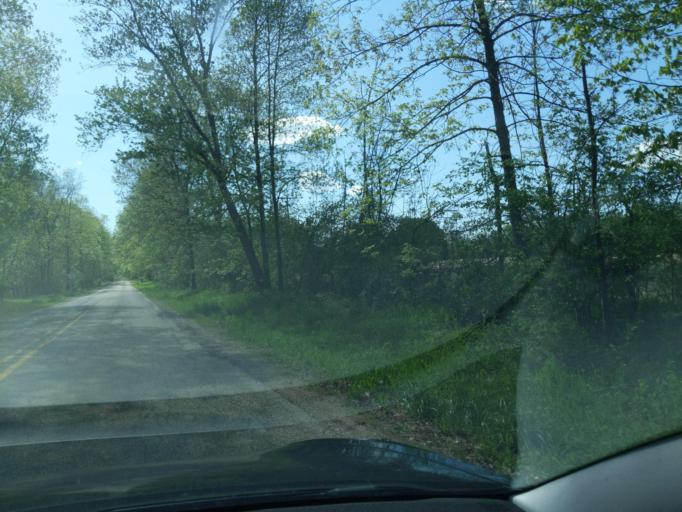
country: US
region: Michigan
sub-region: Kent County
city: Caledonia
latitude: 42.7979
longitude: -85.4588
